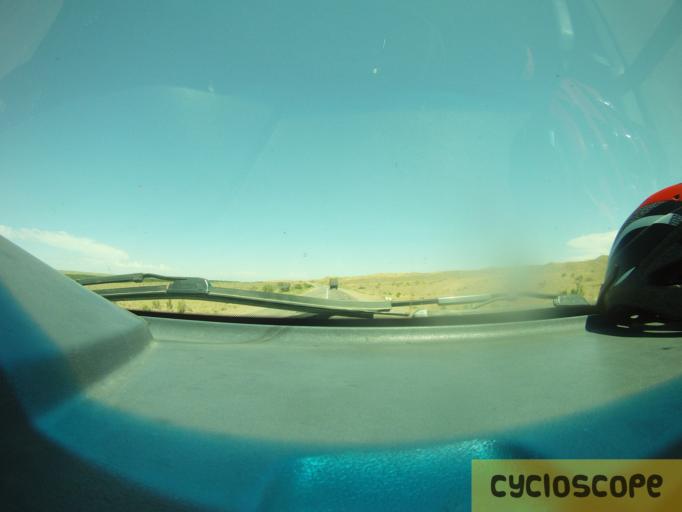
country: KZ
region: Almaty Oblysy
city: Kegen
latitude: 43.5329
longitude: 79.2930
